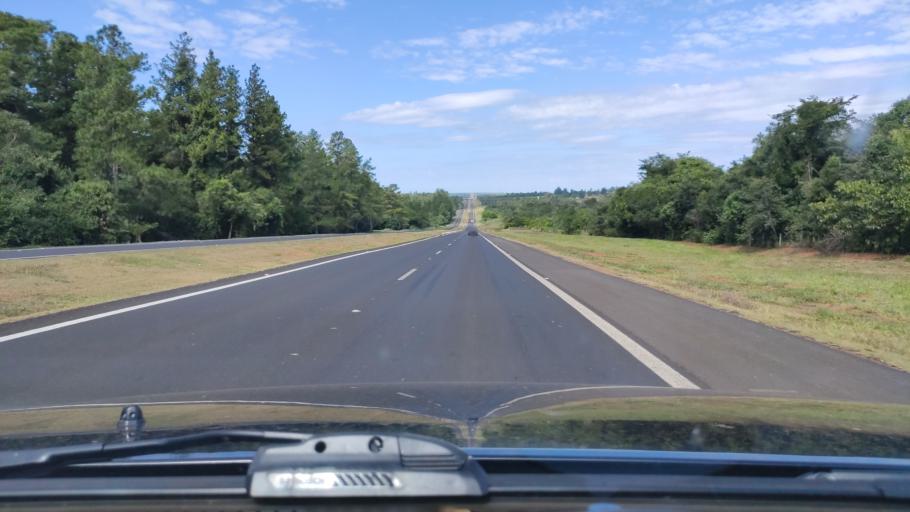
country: BR
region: Sao Paulo
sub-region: Rancharia
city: Rancharia
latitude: -22.4673
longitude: -50.9523
